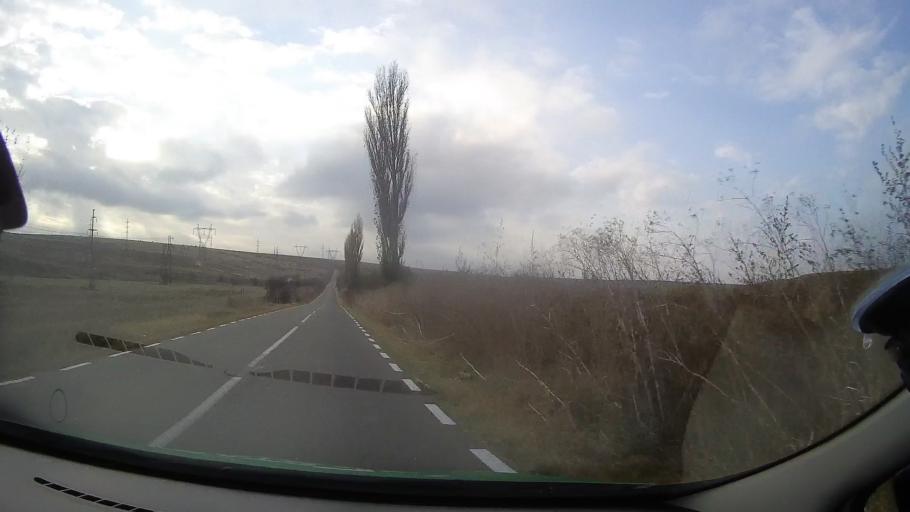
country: RO
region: Constanta
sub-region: Comuna Mircea Voda
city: Satu Nou
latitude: 44.2352
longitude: 28.2270
